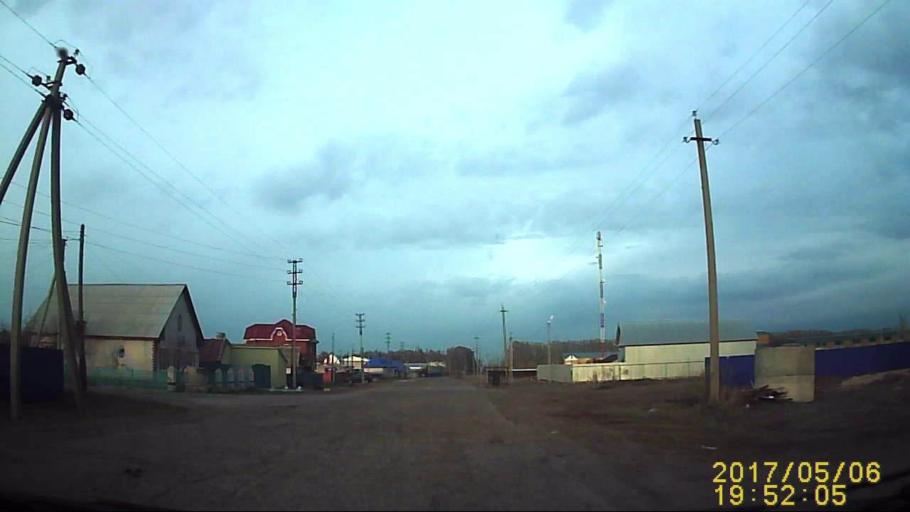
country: RU
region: Ulyanovsk
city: Staraya Mayna
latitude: 54.5988
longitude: 48.9359
